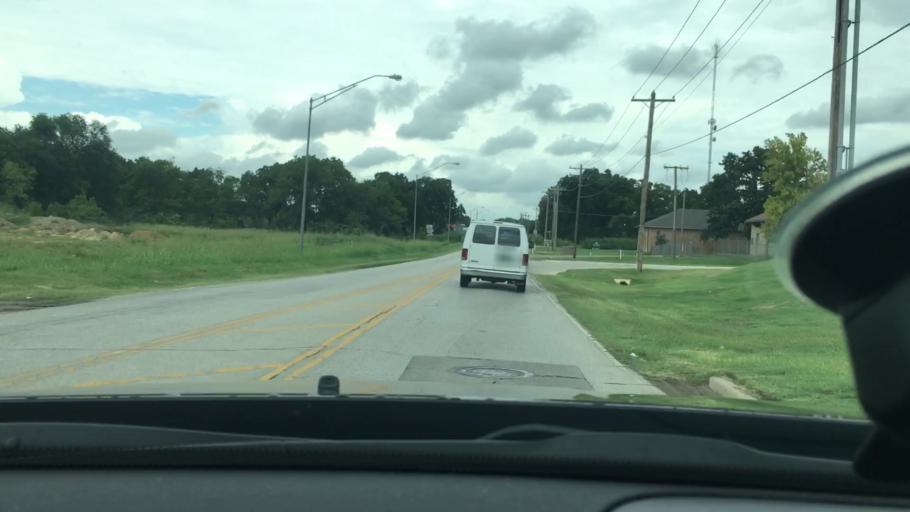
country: US
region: Oklahoma
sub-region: Carter County
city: Ardmore
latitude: 34.1736
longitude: -97.1605
